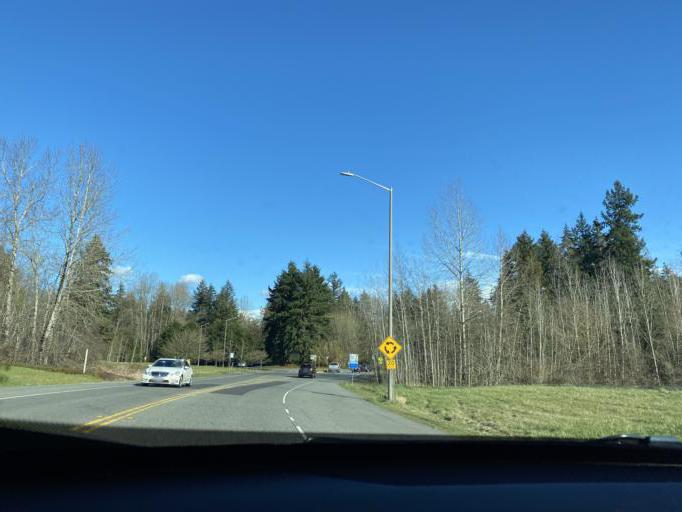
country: US
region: Washington
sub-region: King County
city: Federal Way
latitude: 47.3027
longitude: -122.2986
